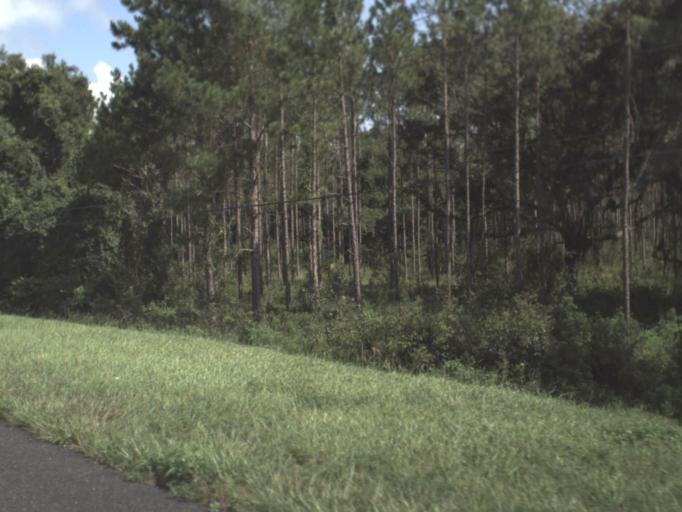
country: US
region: Florida
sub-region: Hernando County
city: Hill 'n Dale
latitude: 28.5247
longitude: -82.3117
